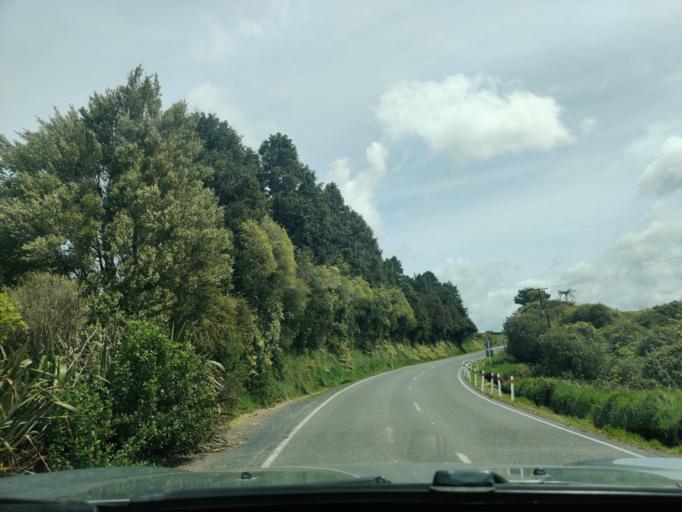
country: NZ
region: Taranaki
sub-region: South Taranaki District
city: Eltham
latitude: -39.3772
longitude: 174.1711
